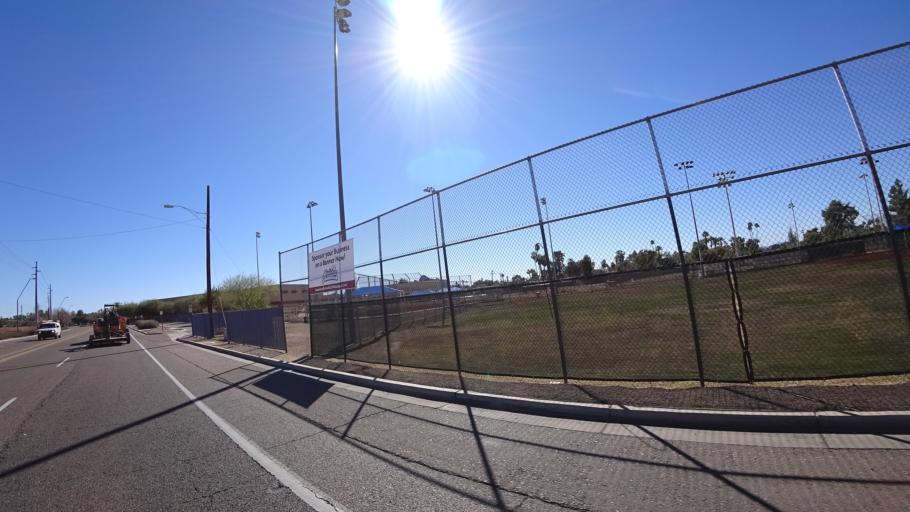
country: US
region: Arizona
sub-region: Maricopa County
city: Paradise Valley
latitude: 33.4902
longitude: -111.9655
